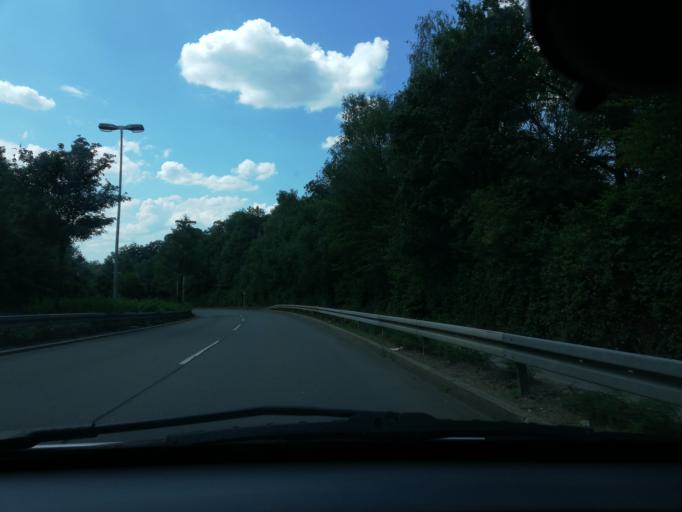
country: DE
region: North Rhine-Westphalia
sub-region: Regierungsbezirk Dusseldorf
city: Wuppertal
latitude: 51.2435
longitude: 7.1763
